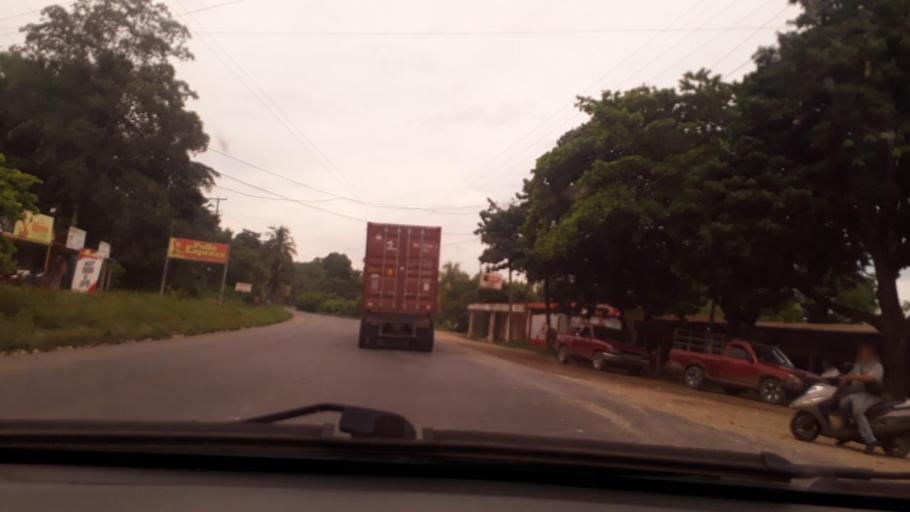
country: GT
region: Izabal
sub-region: Municipio de Puerto Barrios
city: Puerto Barrios
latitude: 15.5936
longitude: -88.5733
